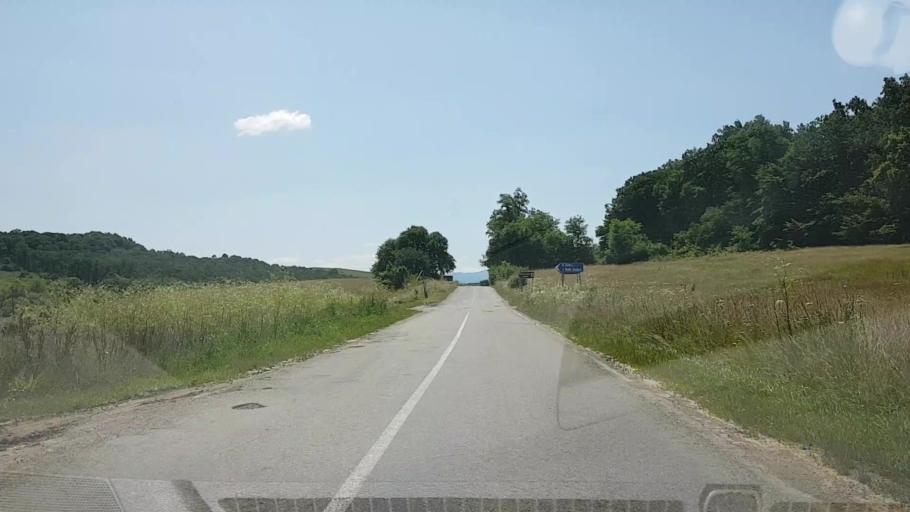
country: RO
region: Brasov
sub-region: Comuna Cincu
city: Cincu
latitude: 45.8704
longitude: 24.8217
